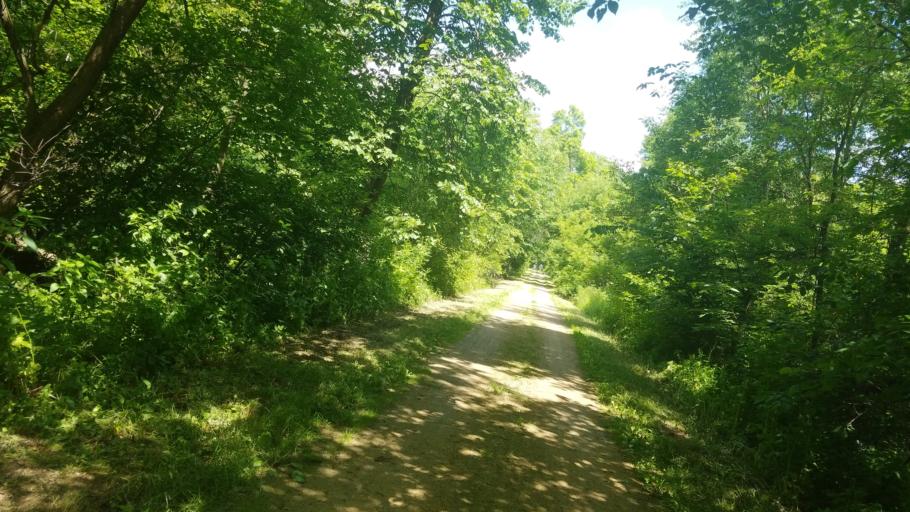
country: US
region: Wisconsin
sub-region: Dunn County
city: Menomonie
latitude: 44.7814
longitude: -91.9418
